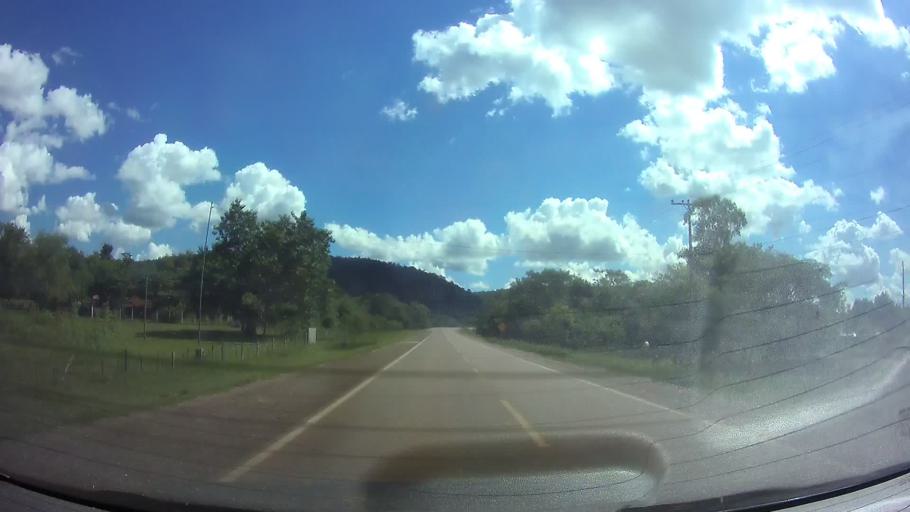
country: PY
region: Paraguari
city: La Colmena
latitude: -25.9161
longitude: -56.7176
